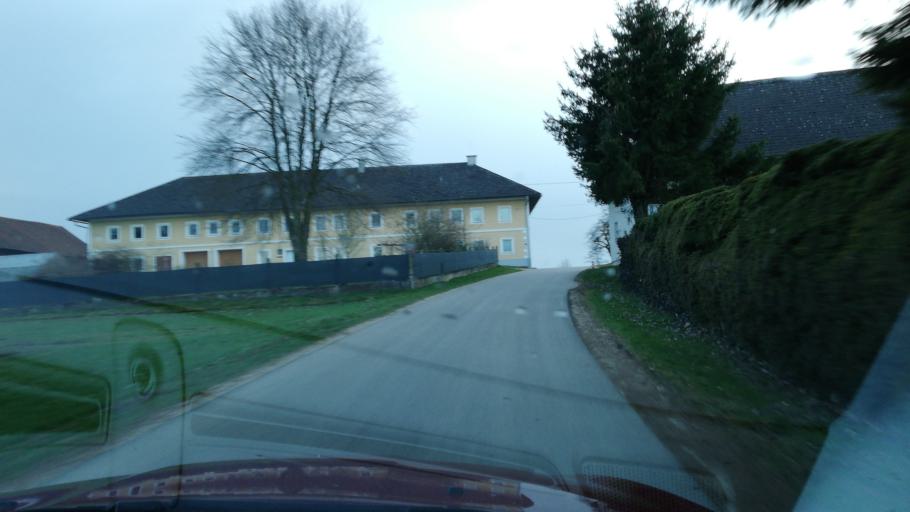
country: AT
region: Upper Austria
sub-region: Wels-Land
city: Holzhausen
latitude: 48.2148
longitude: 14.0629
